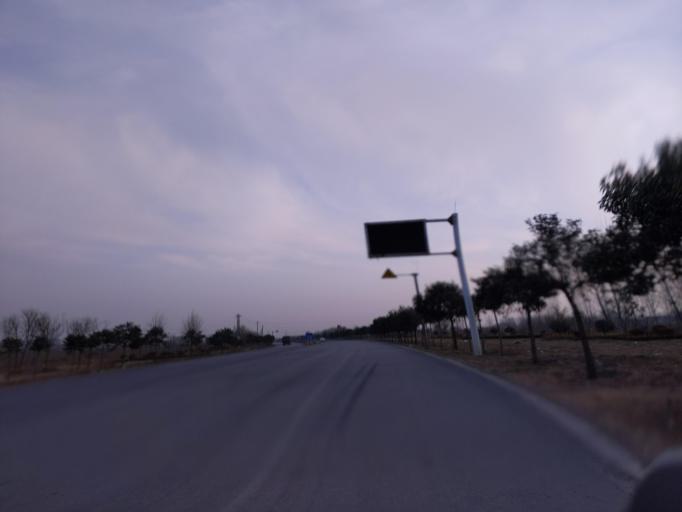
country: CN
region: Henan Sheng
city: Puyang
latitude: 35.8128
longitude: 114.9667
